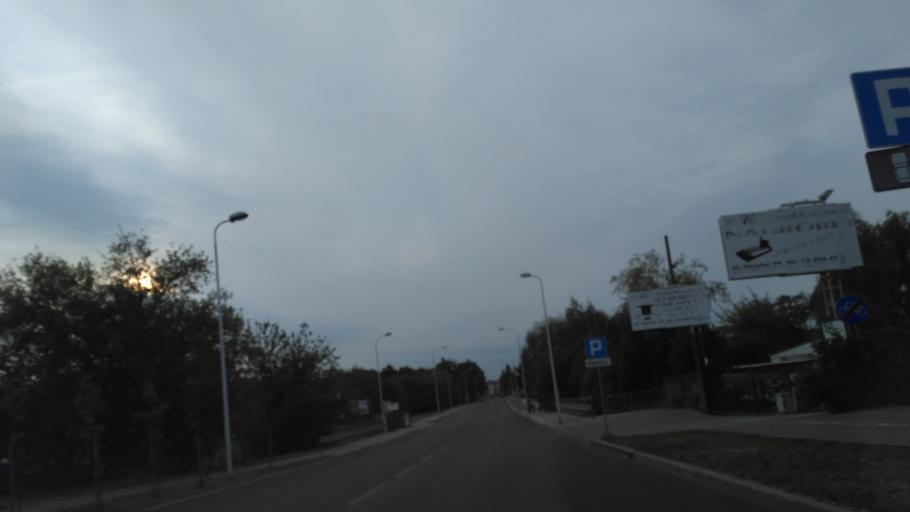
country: PL
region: Lublin Voivodeship
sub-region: Powiat lubelski
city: Lublin
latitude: 51.2067
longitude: 22.5957
